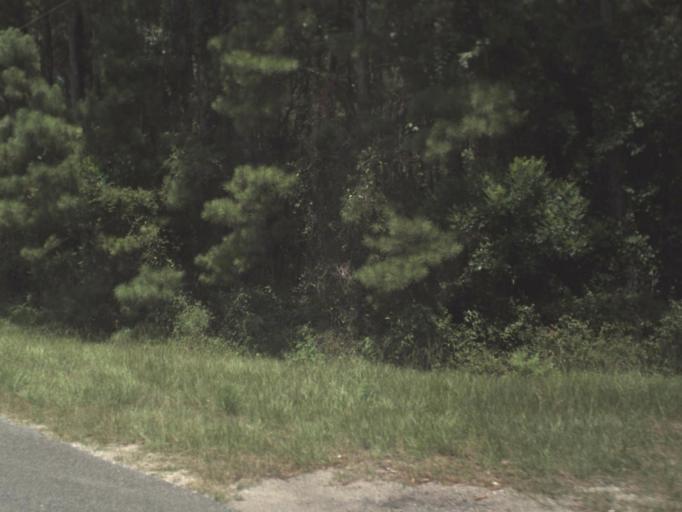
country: US
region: Florida
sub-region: Taylor County
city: Perry
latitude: 30.1005
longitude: -83.6194
